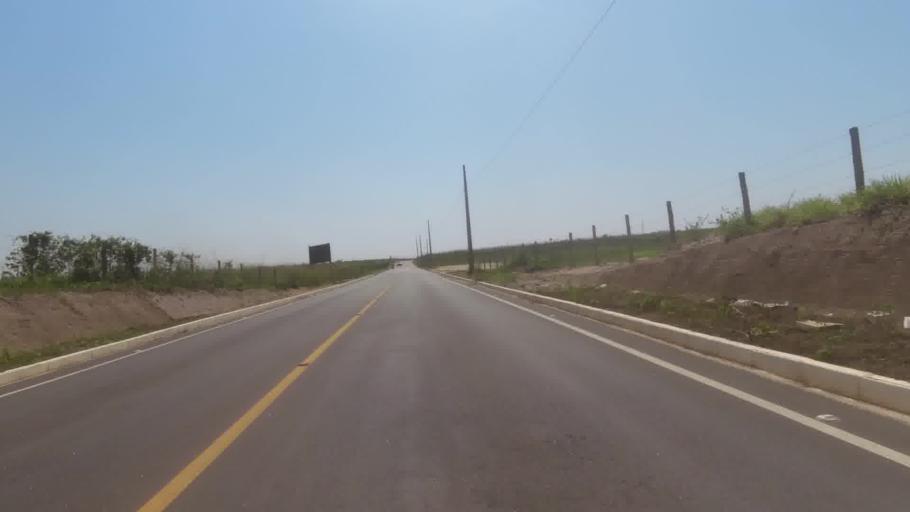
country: BR
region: Espirito Santo
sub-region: Marataizes
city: Marataizes
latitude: -21.0408
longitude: -40.8440
